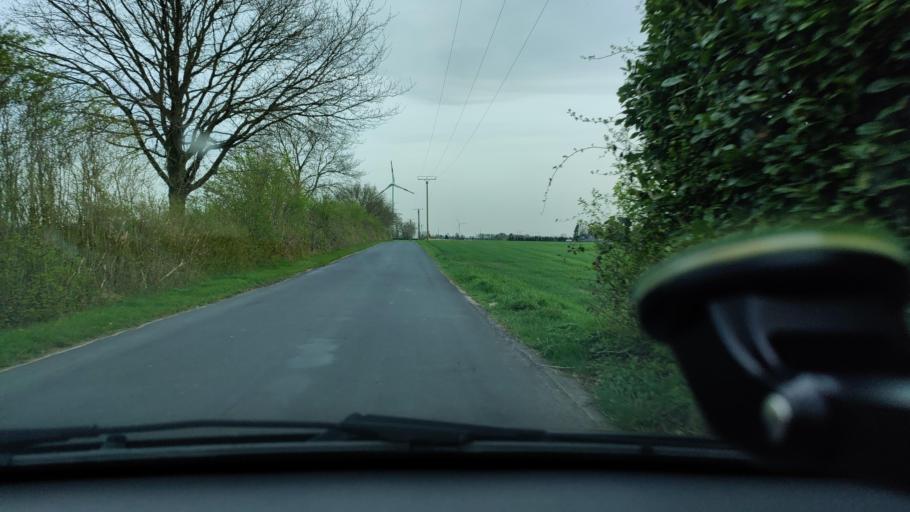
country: DE
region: North Rhine-Westphalia
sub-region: Regierungsbezirk Dusseldorf
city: Goch
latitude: 51.7327
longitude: 6.1950
